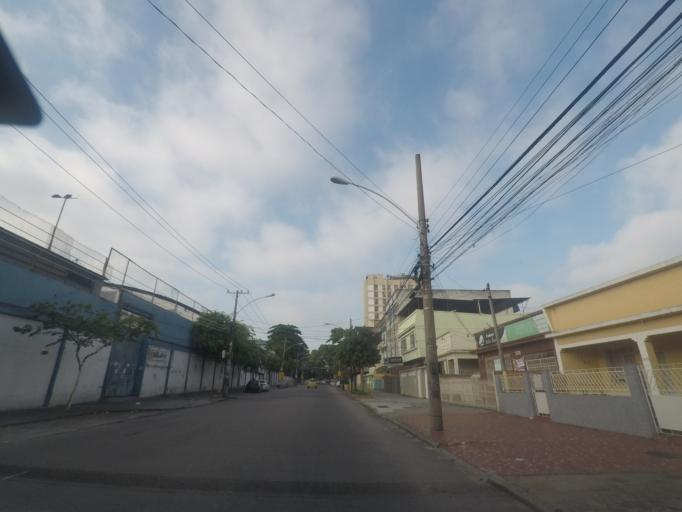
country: BR
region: Rio de Janeiro
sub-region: Duque De Caxias
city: Duque de Caxias
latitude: -22.8409
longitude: -43.2675
